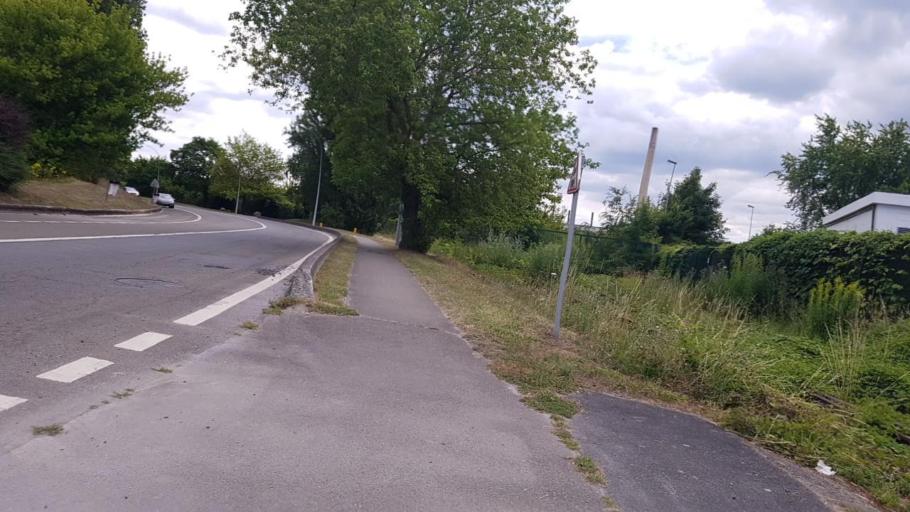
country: FR
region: Picardie
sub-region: Departement de l'Oise
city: Clairoix
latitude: 49.4329
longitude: 2.8528
